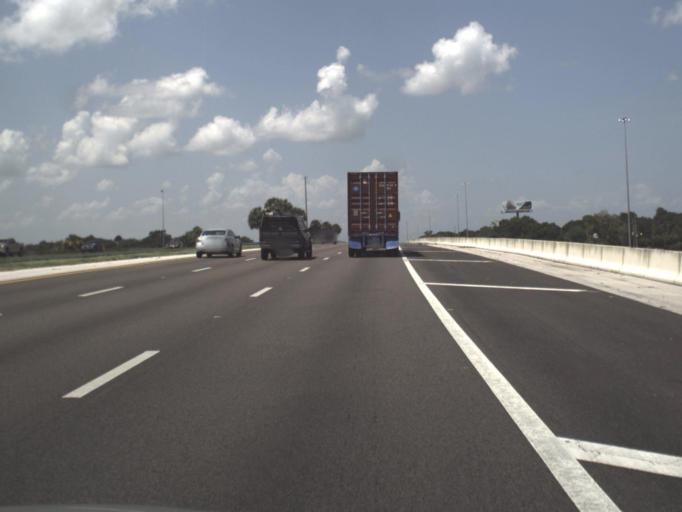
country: US
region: Florida
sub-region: Hillsborough County
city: Plant City
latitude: 28.0275
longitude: -82.1505
